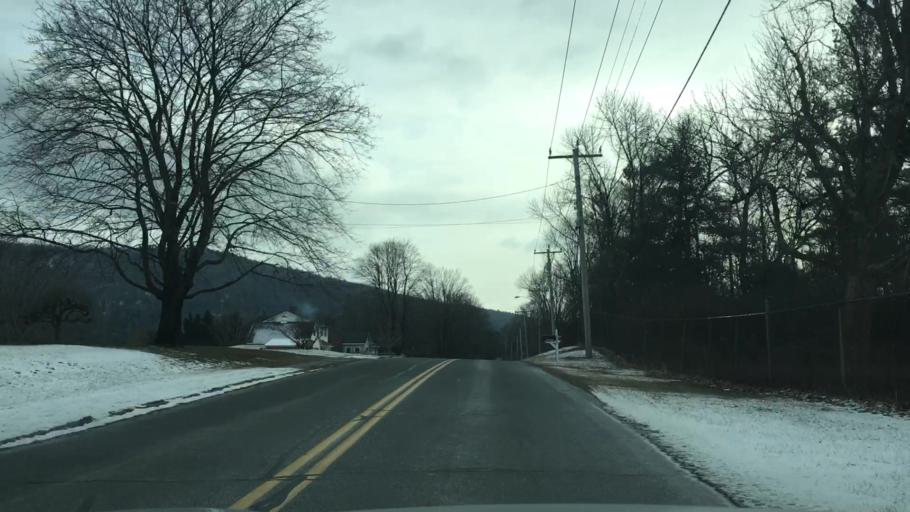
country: US
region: Massachusetts
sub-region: Berkshire County
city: Lee
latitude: 42.2963
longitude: -73.2482
